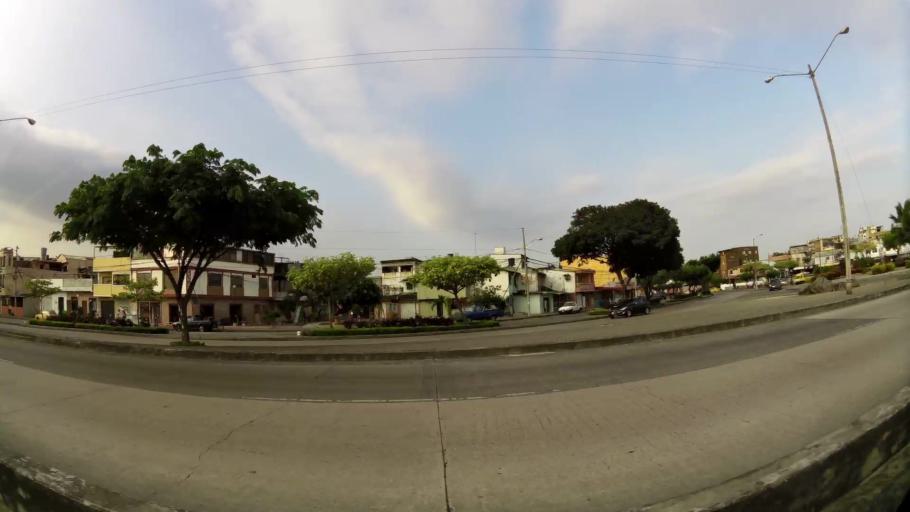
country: EC
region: Guayas
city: Eloy Alfaro
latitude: -2.1302
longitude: -79.8982
